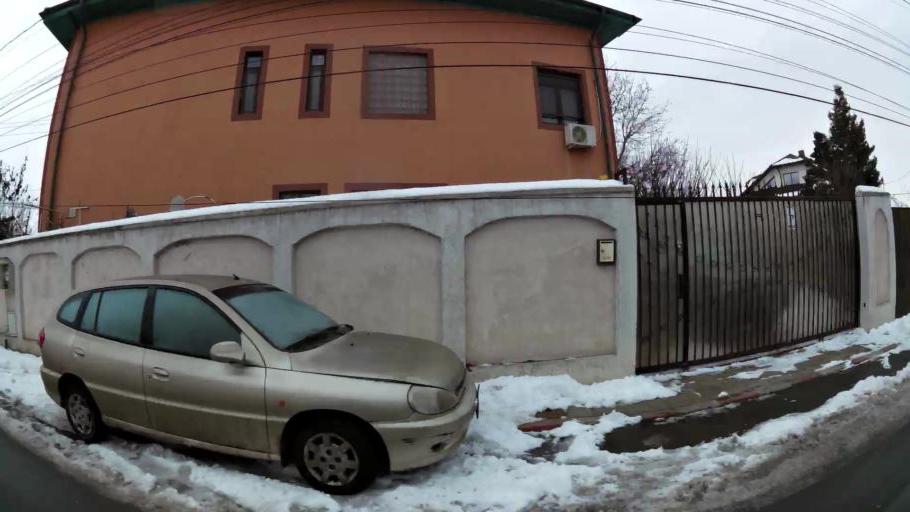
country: RO
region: Ilfov
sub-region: Comuna Tunari
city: Tunari
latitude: 44.5110
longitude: 26.1099
